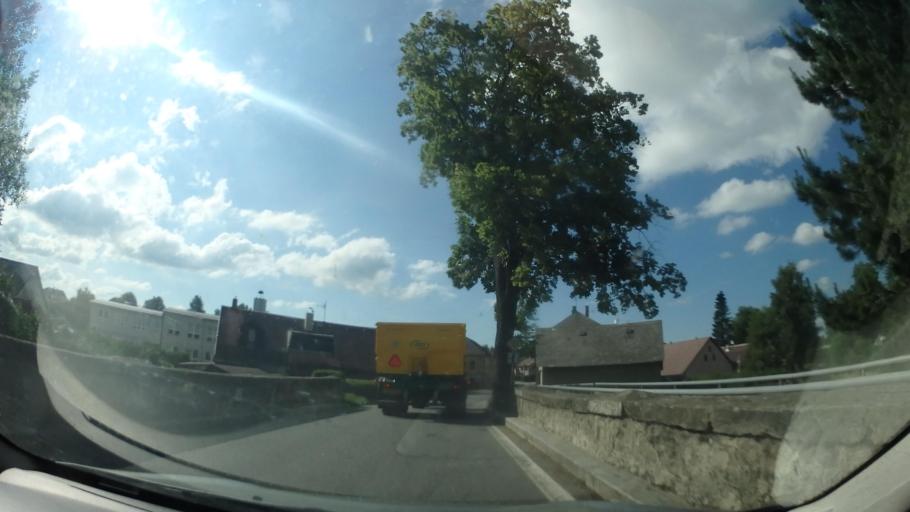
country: CZ
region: Vysocina
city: Heralec
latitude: 49.6894
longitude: 15.9926
